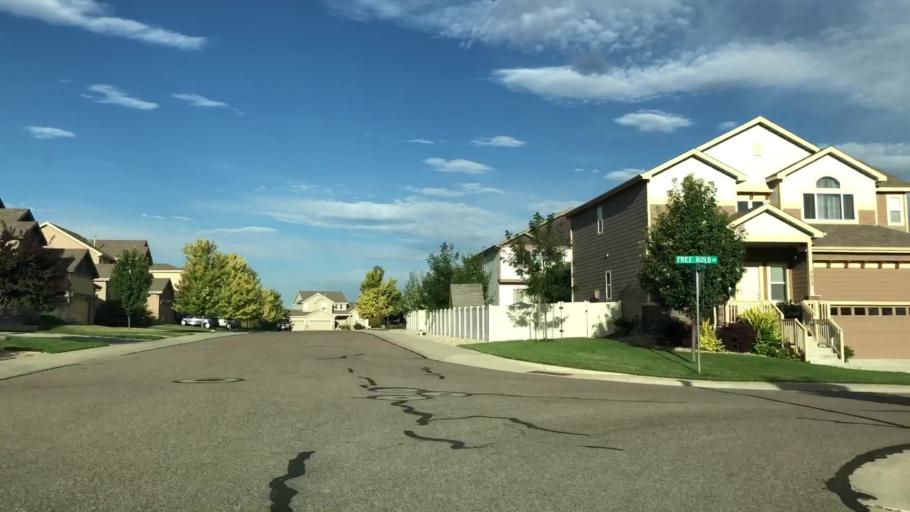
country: US
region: Colorado
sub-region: Weld County
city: Windsor
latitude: 40.4405
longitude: -104.9649
